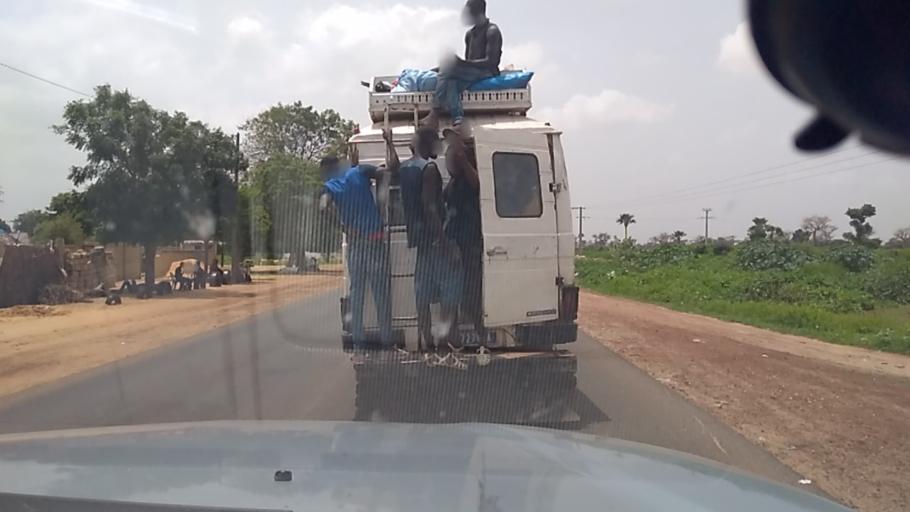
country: SN
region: Thies
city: Mekhe
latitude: 15.0185
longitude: -16.7374
